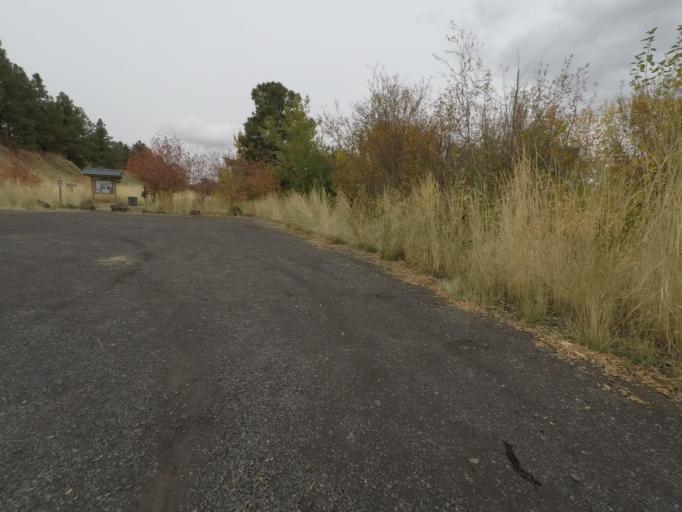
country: US
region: Washington
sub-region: Walla Walla County
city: Walla Walla East
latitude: 46.0676
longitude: -118.2640
